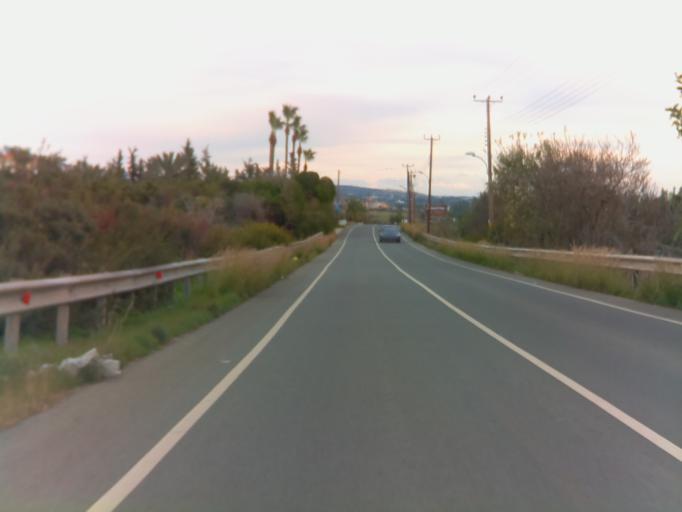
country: CY
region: Pafos
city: Pegeia
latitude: 34.8709
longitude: 32.3620
